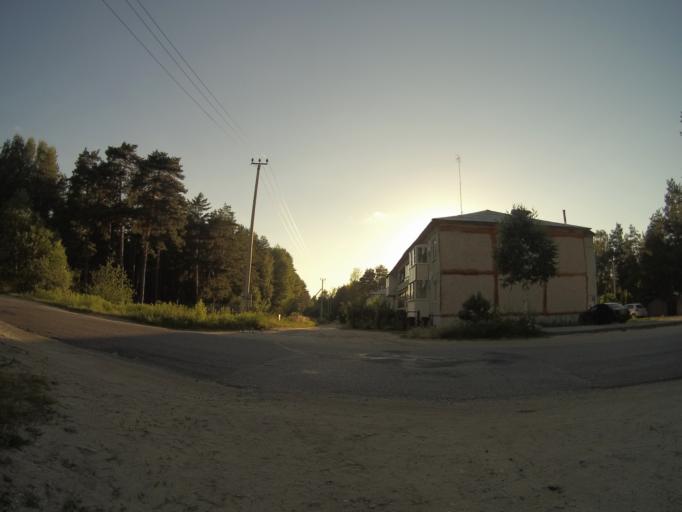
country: RU
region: Vladimir
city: Kommunar
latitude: 56.1389
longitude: 40.4919
